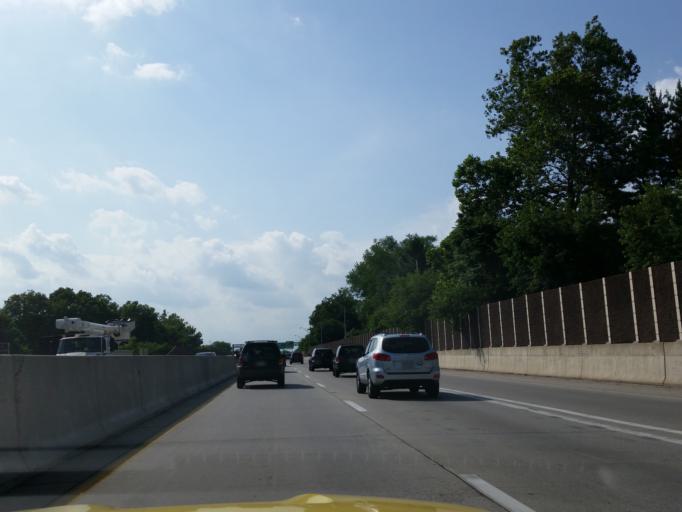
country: US
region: Pennsylvania
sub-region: Lancaster County
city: Lancaster
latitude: 40.0629
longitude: -76.2809
